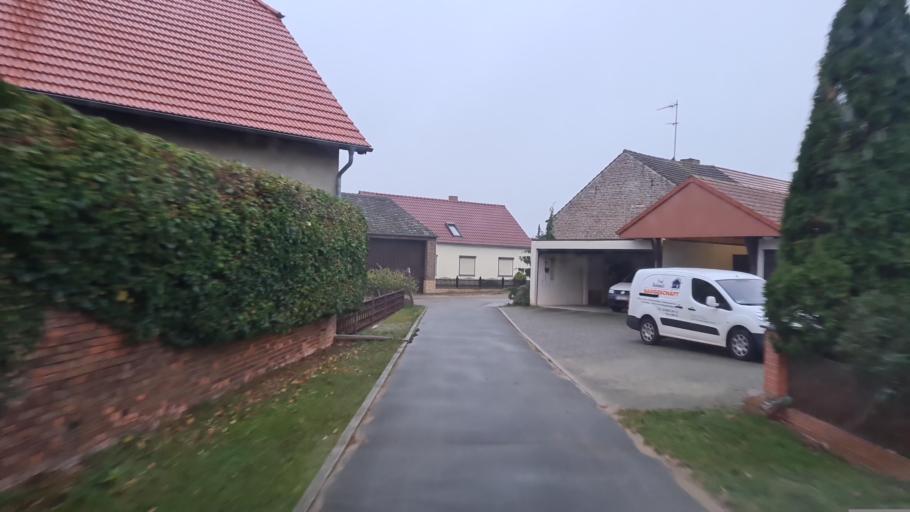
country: DE
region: Brandenburg
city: Beelitz
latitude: 52.2453
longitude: 13.0193
